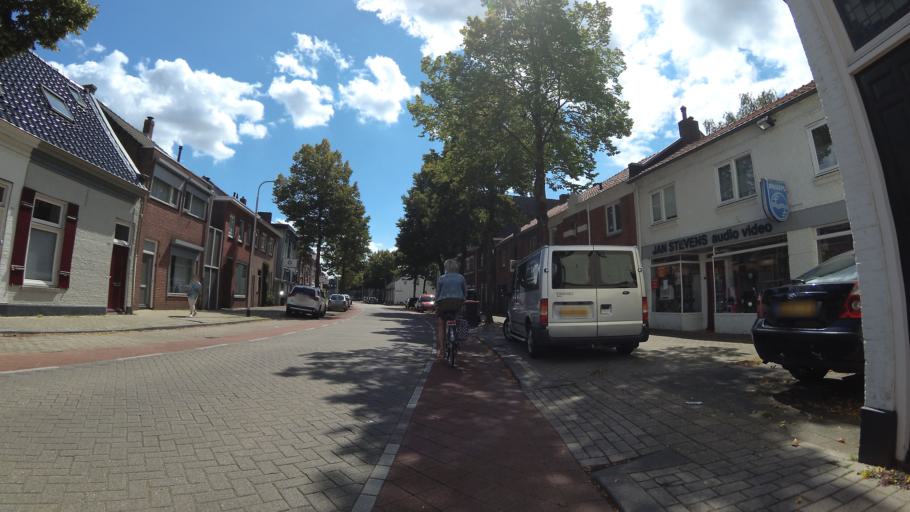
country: NL
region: North Brabant
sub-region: Gemeente Goirle
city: Goirle
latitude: 51.5492
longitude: 5.0624
